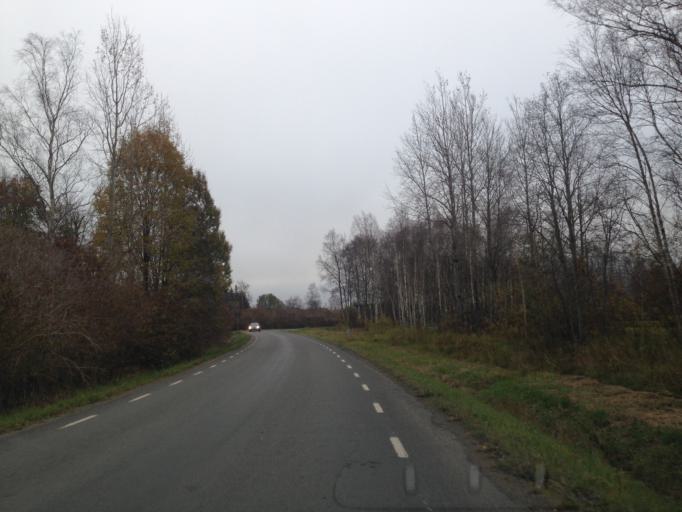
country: EE
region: Harju
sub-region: Saue linn
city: Saue
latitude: 59.3734
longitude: 24.5413
